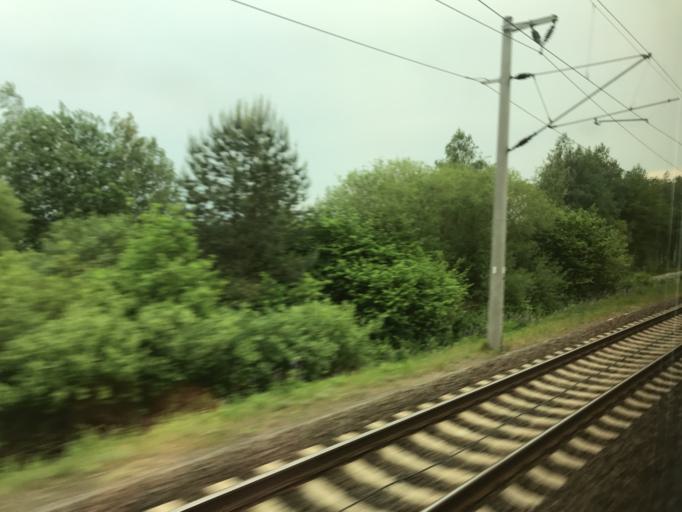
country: DE
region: Saxony-Anhalt
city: Mieste
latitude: 52.4991
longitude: 11.2878
